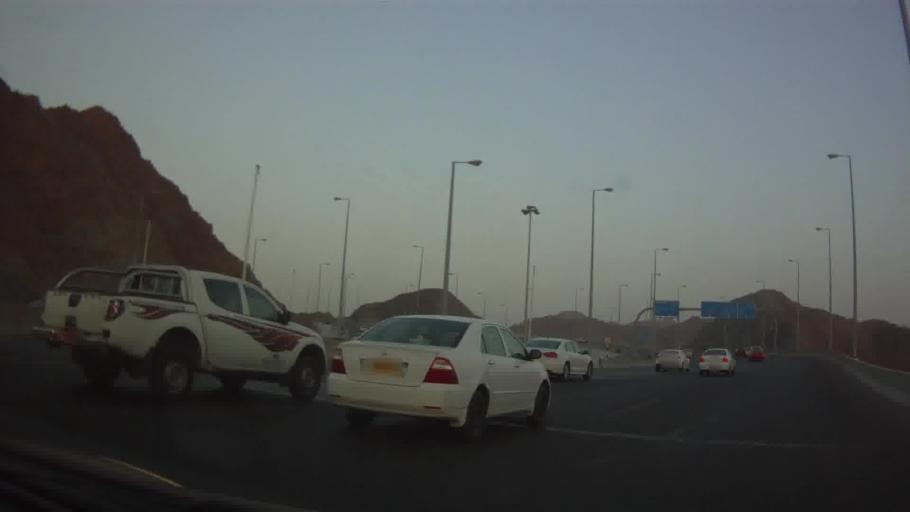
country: OM
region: Muhafazat Masqat
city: Muscat
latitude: 23.6194
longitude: 58.5405
